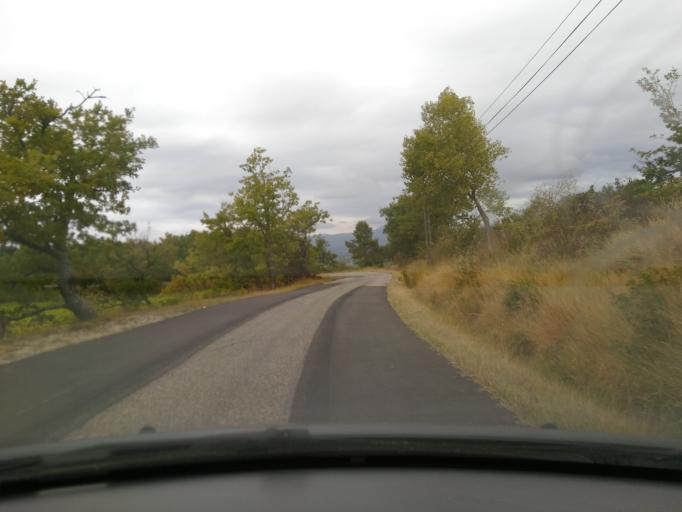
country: FR
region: Provence-Alpes-Cote d'Azur
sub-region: Departement du Vaucluse
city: Valreas
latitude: 44.3631
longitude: 5.0162
